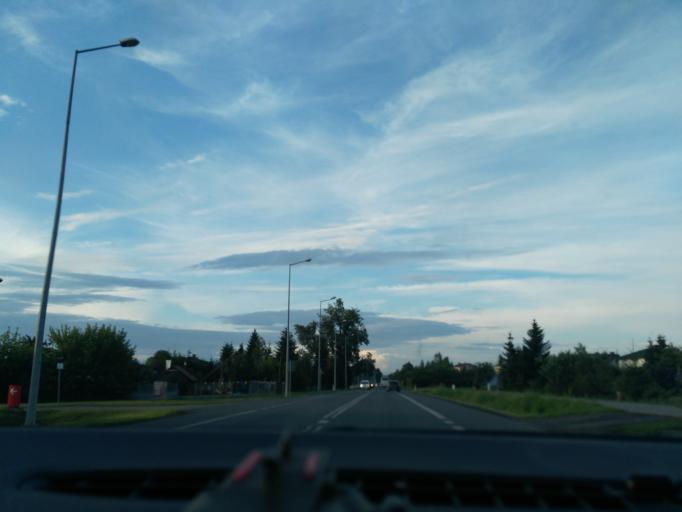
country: PL
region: Lublin Voivodeship
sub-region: Powiat lubelski
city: Niedrzwica Duza
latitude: 51.0951
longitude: 22.3677
